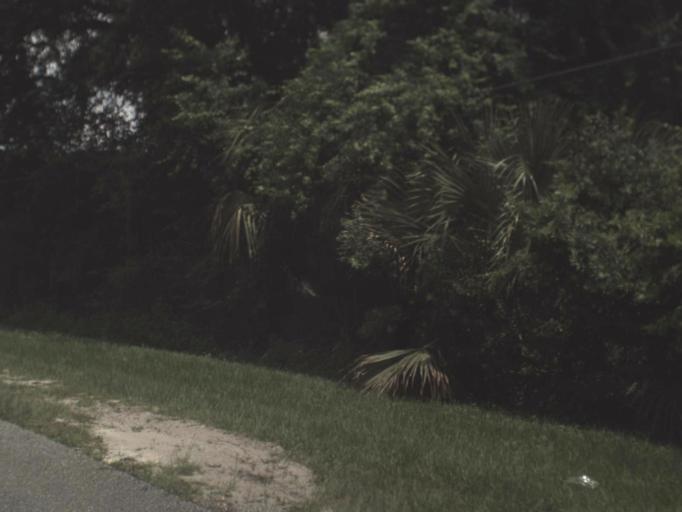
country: US
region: Florida
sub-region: Putnam County
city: Palatka
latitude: 29.5978
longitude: -81.7116
